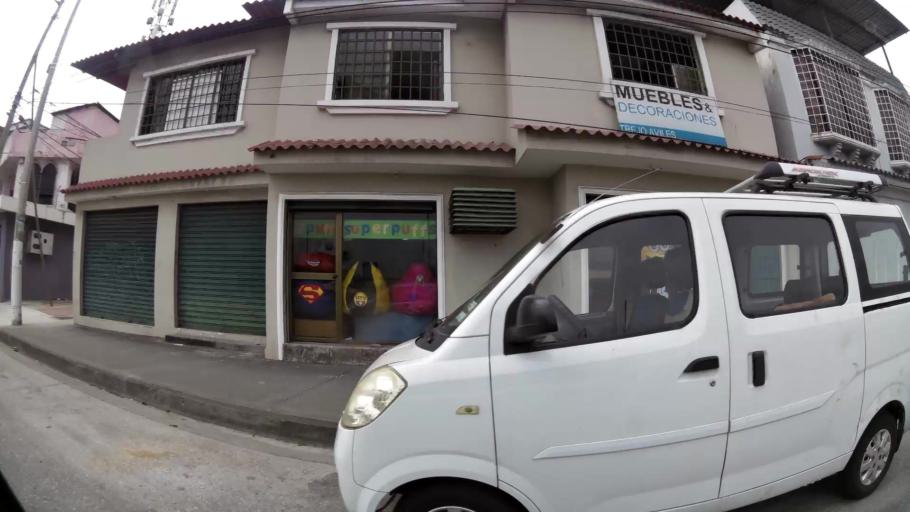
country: EC
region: Guayas
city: Eloy Alfaro
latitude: -2.1526
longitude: -79.8960
